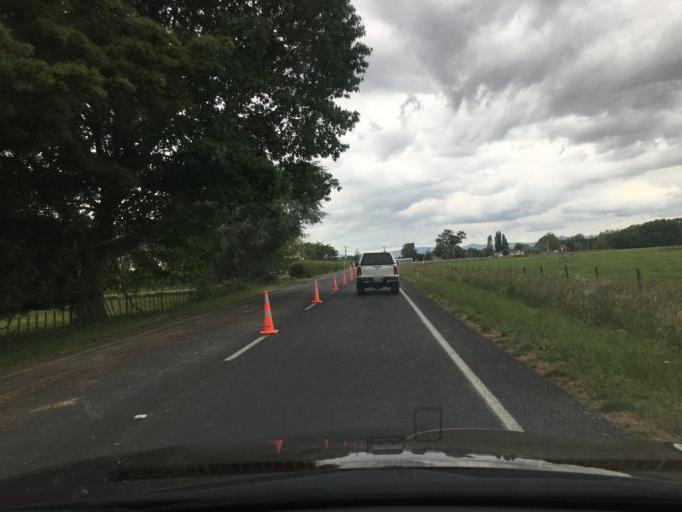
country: NZ
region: Waikato
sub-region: Waipa District
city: Cambridge
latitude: -37.9208
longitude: 175.4370
